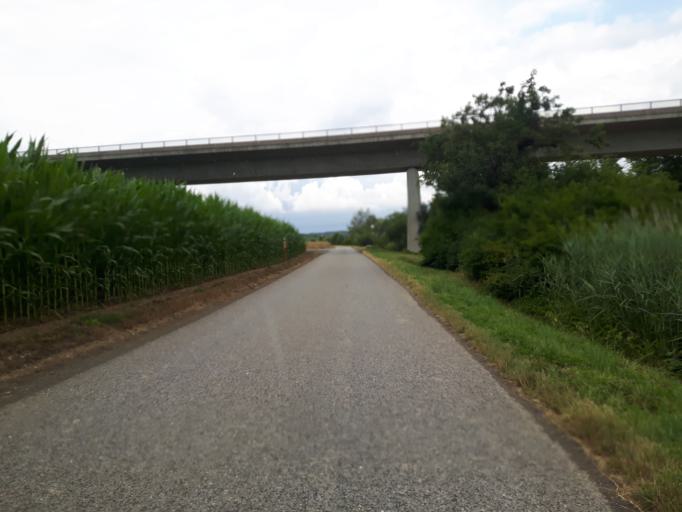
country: DE
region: Baden-Wuerttemberg
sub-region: Regierungsbezirk Stuttgart
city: Eppingen
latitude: 49.1427
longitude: 8.9263
